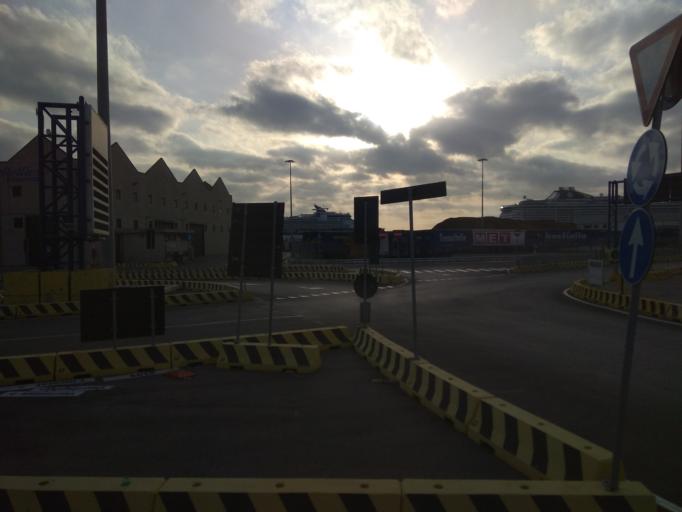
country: IT
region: Latium
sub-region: Citta metropolitana di Roma Capitale
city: Civitavecchia
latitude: 42.1029
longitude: 11.7820
